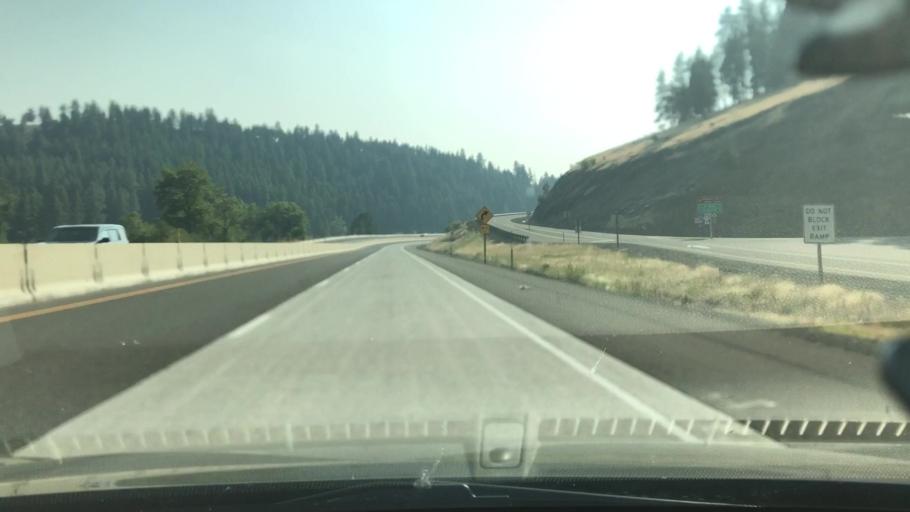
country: US
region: Oregon
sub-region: Union County
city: La Grande
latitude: 45.3448
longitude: -118.2253
